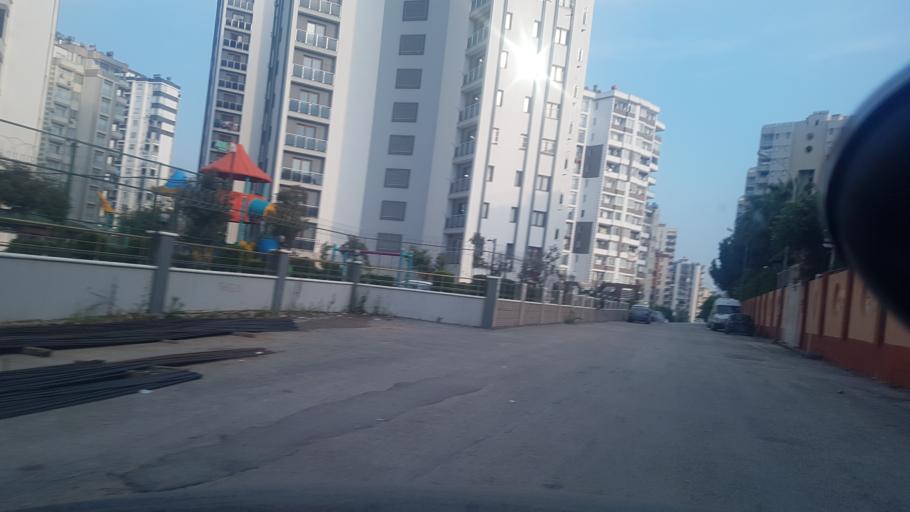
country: TR
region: Adana
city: Seyhan
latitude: 37.0459
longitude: 35.2763
